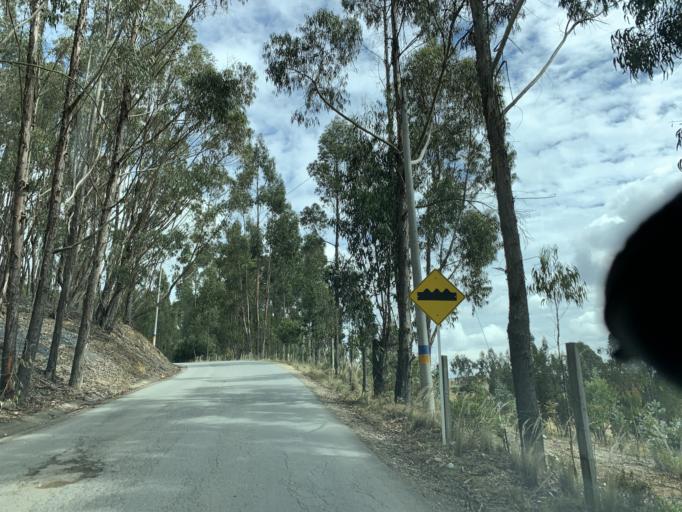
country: CO
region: Boyaca
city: Siachoque
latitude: 5.5695
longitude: -73.2666
